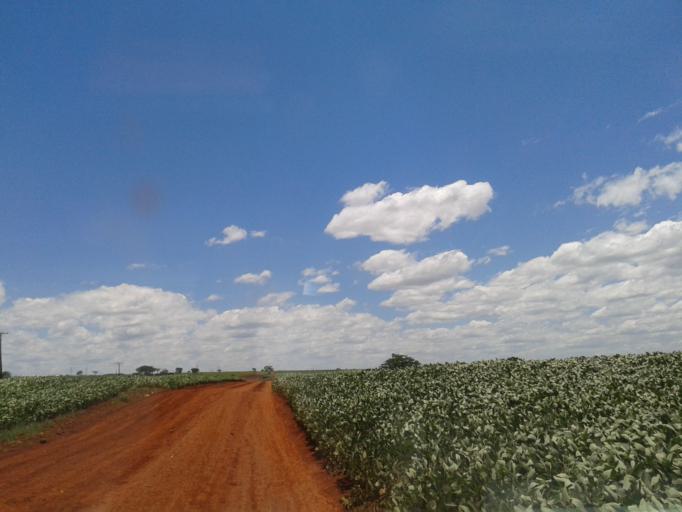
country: BR
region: Minas Gerais
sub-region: Centralina
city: Centralina
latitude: -18.6970
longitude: -49.2183
